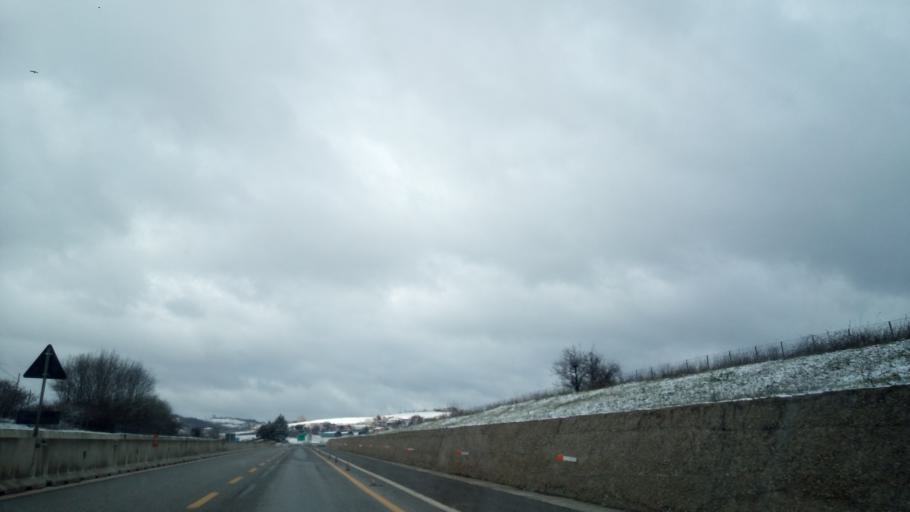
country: IT
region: Campania
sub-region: Provincia di Avellino
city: Scampitella
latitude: 41.0621
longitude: 15.3039
